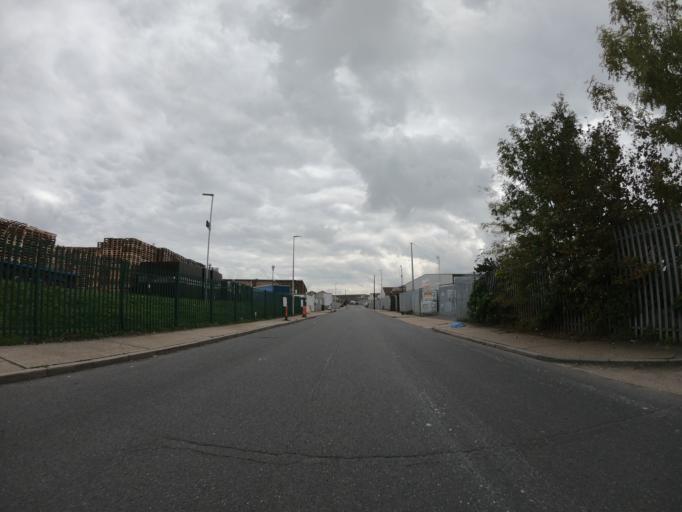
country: GB
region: England
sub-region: Greater London
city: Belvedere
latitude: 51.5003
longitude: 0.1651
